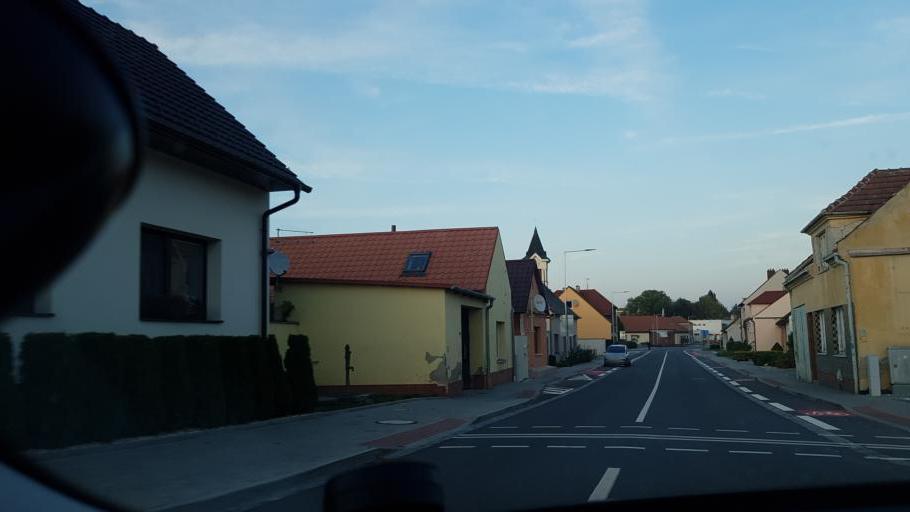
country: CZ
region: Zlin
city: Zlechov
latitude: 49.0719
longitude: 17.3785
